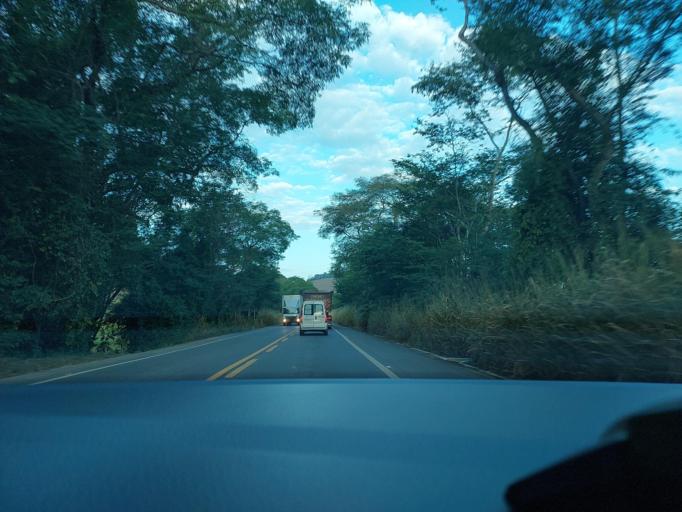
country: BR
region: Minas Gerais
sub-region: Muriae
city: Muriae
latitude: -21.1472
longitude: -42.1651
